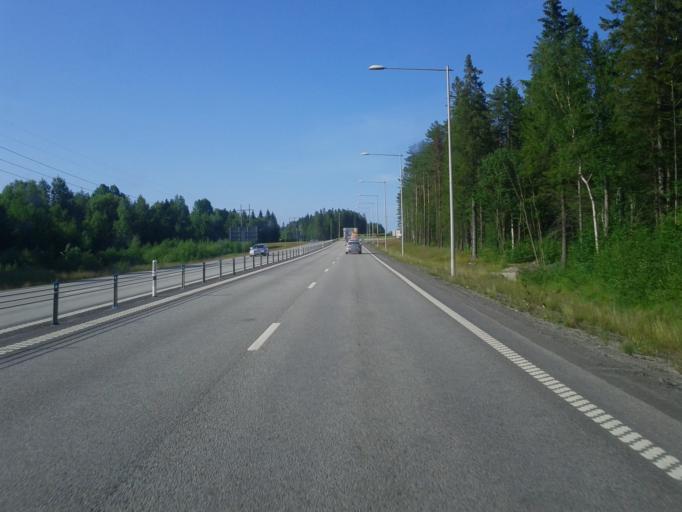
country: SE
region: Vaesterbotten
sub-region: Umea Kommun
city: Umea
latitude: 63.8155
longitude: 20.3271
